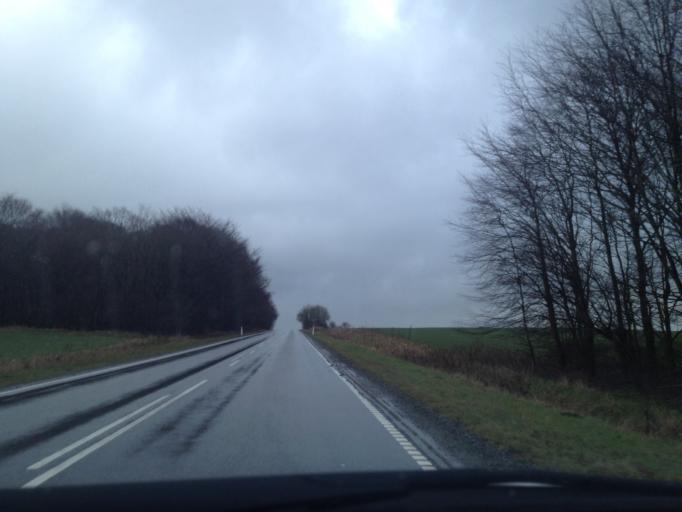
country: DK
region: South Denmark
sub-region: Vejen Kommune
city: Rodding
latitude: 55.3586
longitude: 9.1445
